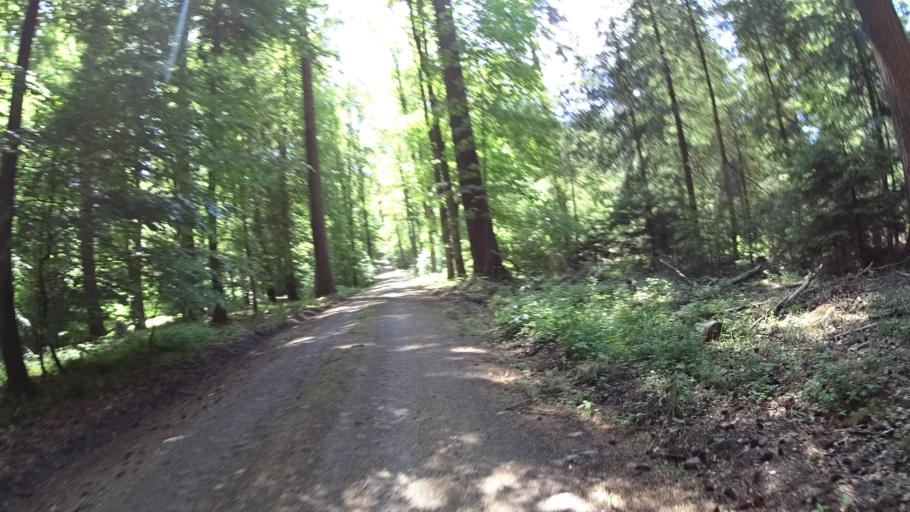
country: DE
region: Baden-Wuerttemberg
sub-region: Karlsruhe Region
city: Schonau
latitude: 49.4222
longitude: 8.7907
